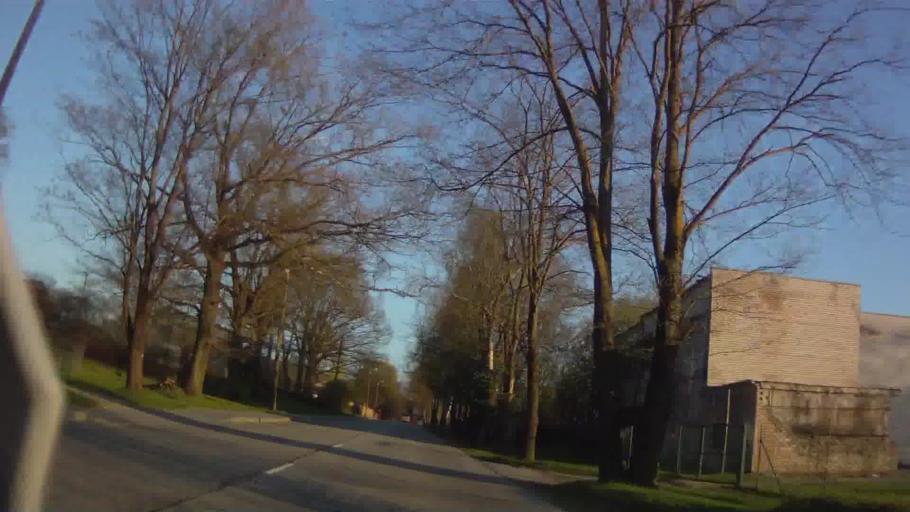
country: LV
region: Riga
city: Jaunciems
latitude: 57.0492
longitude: 24.1729
